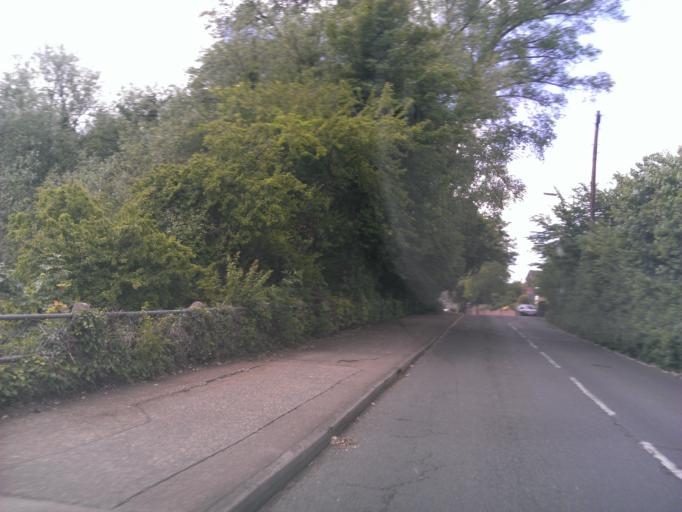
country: GB
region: England
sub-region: Essex
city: Colchester
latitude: 51.8773
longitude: 0.9112
